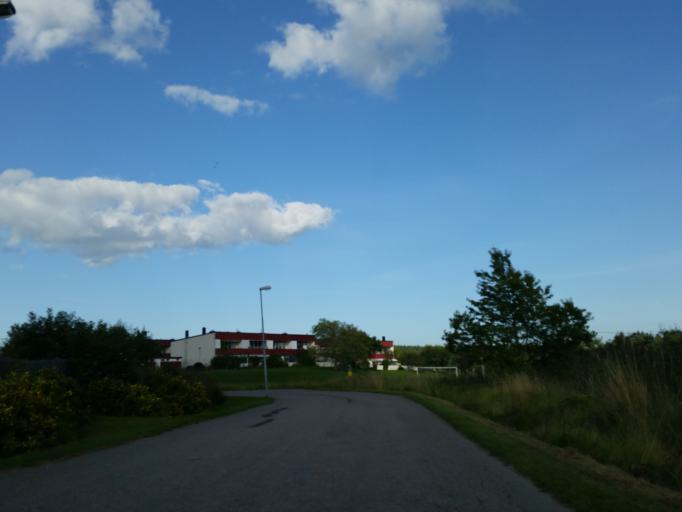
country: SE
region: Soedermanland
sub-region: Trosa Kommun
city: Vagnharad
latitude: 58.9411
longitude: 17.4997
